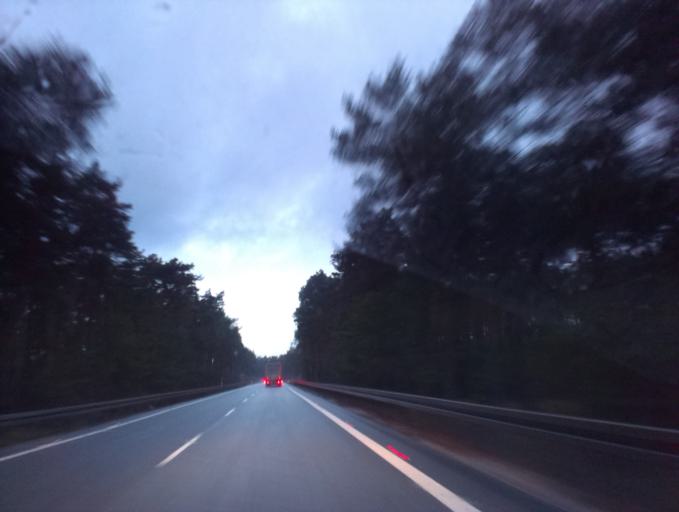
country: PL
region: Swietokrzyskie
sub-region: Powiat konecki
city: Ruda Maleniecka
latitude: 51.1794
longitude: 20.2198
